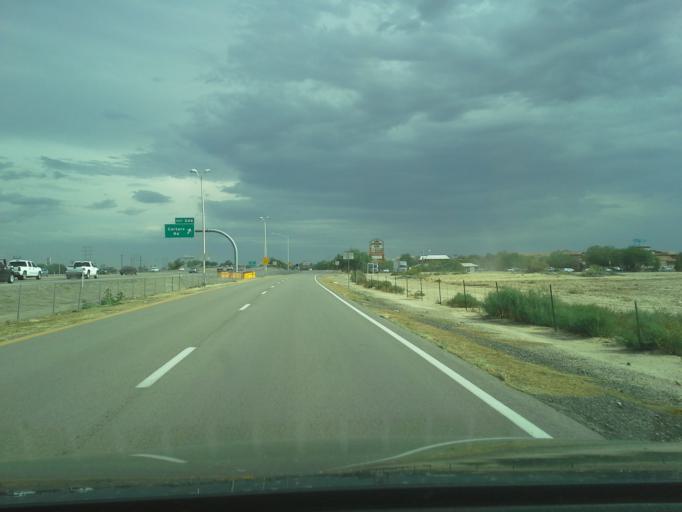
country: US
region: Arizona
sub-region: Pima County
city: Tortolita
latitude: 32.3632
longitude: -111.0949
